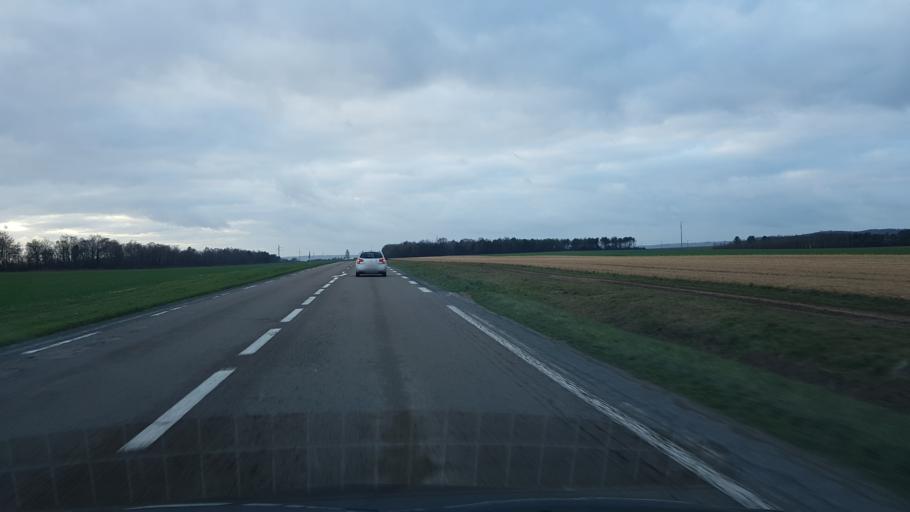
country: FR
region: Champagne-Ardenne
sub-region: Departement de la Marne
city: Connantre
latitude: 48.7290
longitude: 3.8867
